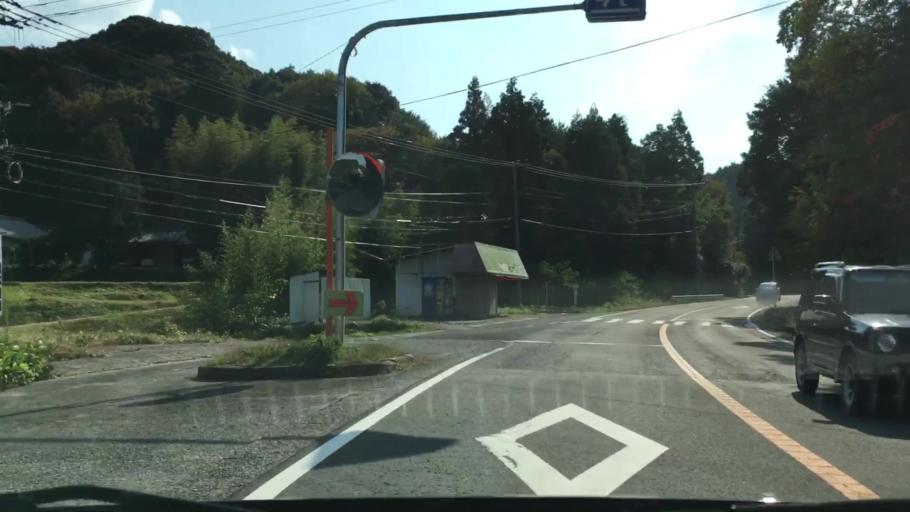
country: JP
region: Nagasaki
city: Togitsu
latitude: 32.9757
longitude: 129.7818
